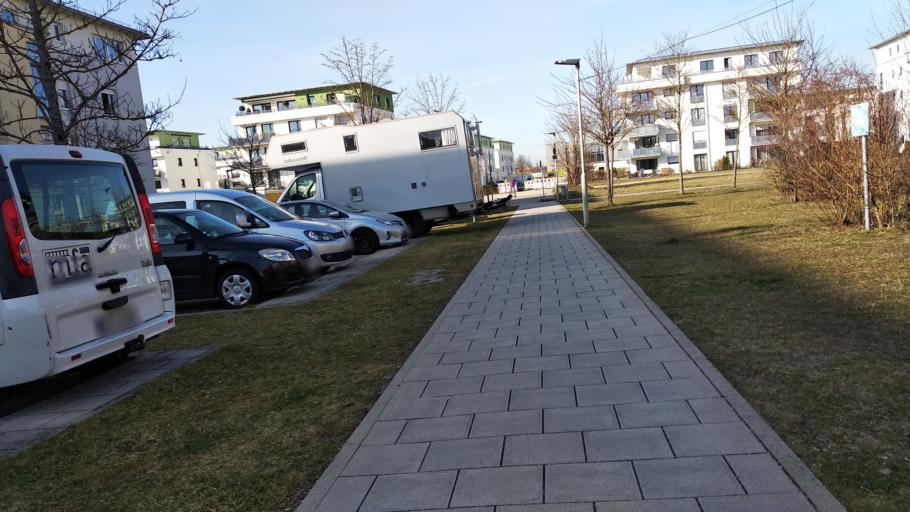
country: DE
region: Bavaria
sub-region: Upper Bavaria
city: Unterhaching
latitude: 48.0695
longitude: 11.6146
